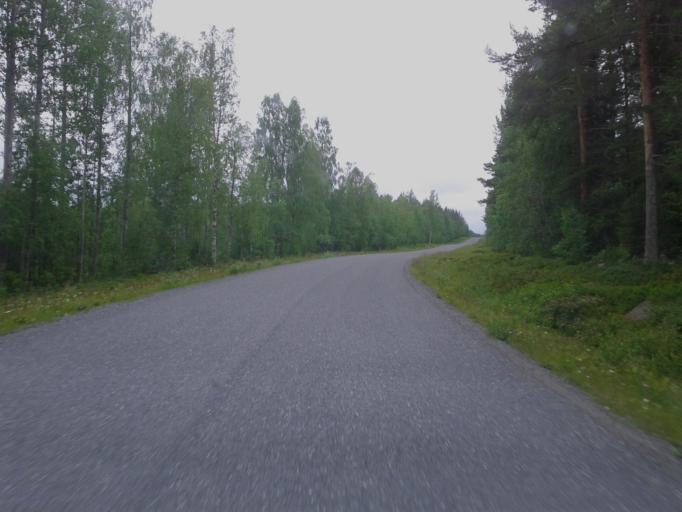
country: SE
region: Vaesterbotten
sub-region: Skelleftea Kommun
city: Storvik
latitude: 65.0040
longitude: 20.7482
